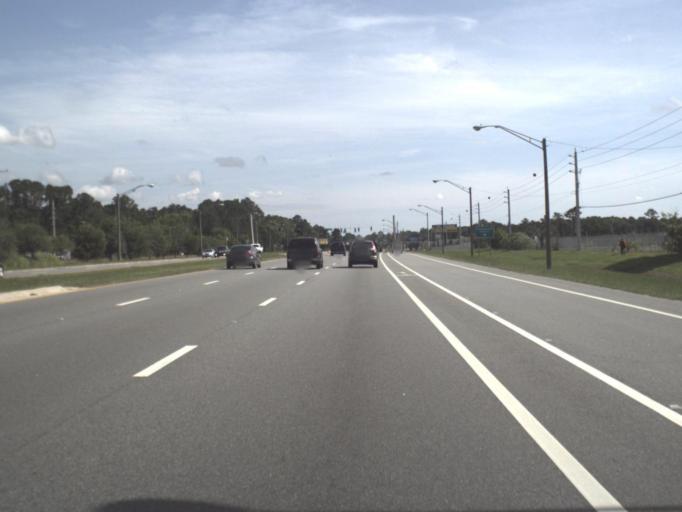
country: US
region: Florida
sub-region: Clay County
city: Orange Park
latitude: 30.2296
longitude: -81.6993
